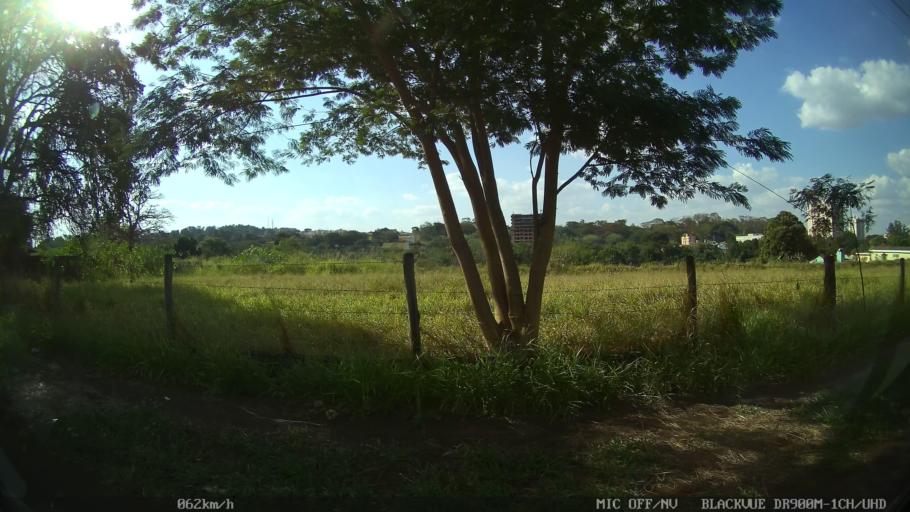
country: BR
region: Sao Paulo
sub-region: Ribeirao Preto
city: Ribeirao Preto
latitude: -21.1768
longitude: -47.8448
